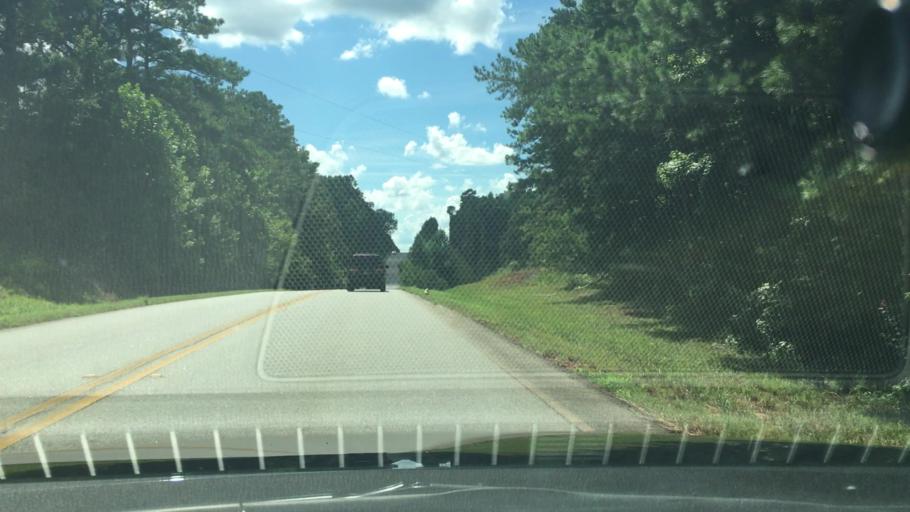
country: US
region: Georgia
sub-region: Jasper County
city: Monticello
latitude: 33.3020
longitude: -83.6382
